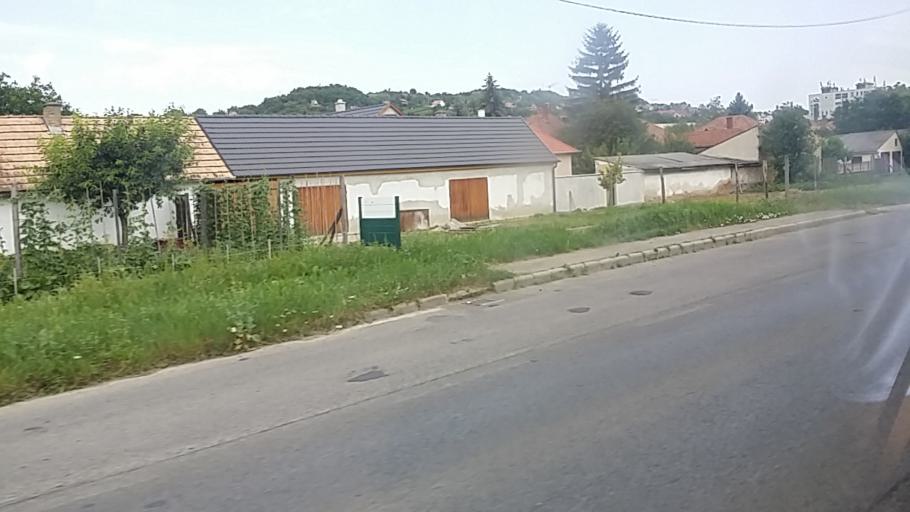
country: HU
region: Tolna
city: Szekszard
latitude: 46.3269
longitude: 18.6988
